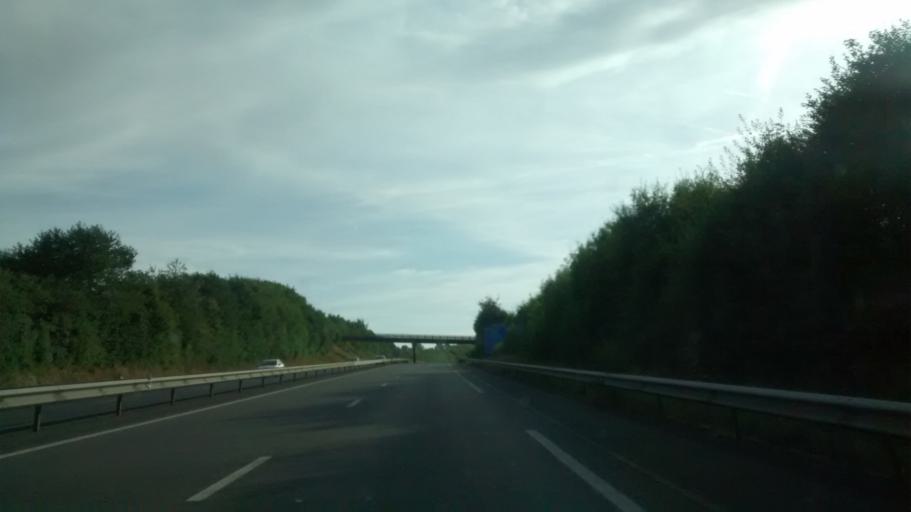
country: FR
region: Lower Normandy
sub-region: Departement du Calvados
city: Saint-Martin-des-Besaces
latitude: 49.0193
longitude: -0.8431
